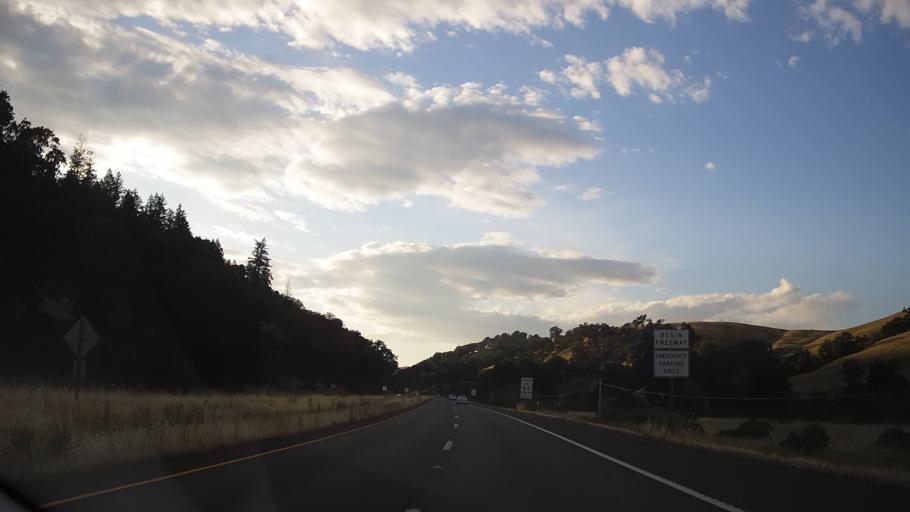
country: US
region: California
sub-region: Mendocino County
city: Talmage
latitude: 39.0582
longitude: -123.1597
